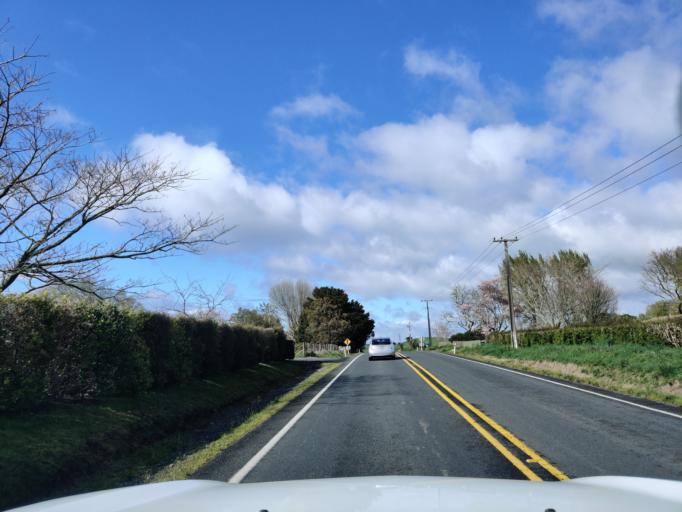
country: NZ
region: Waikato
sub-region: Otorohanga District
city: Otorohanga
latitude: -38.1002
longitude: 175.1893
